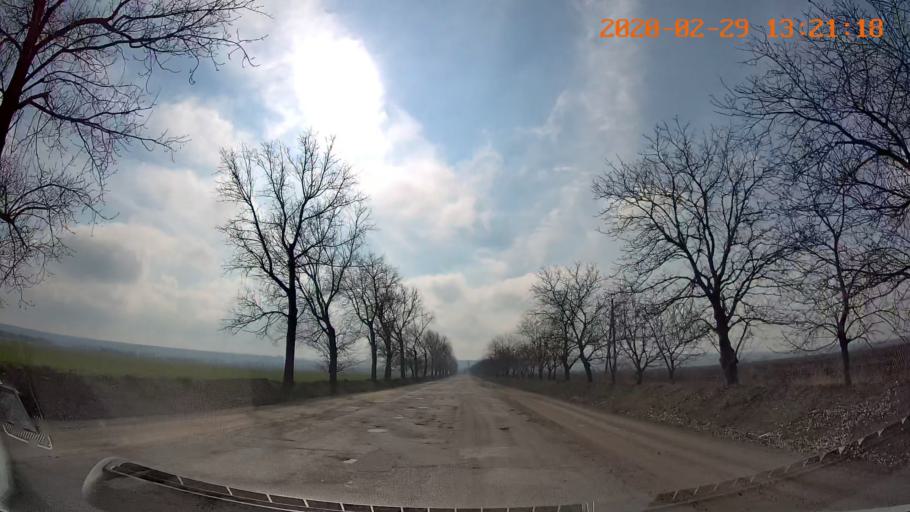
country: MD
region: Telenesti
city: Camenca
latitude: 47.9714
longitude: 28.6341
